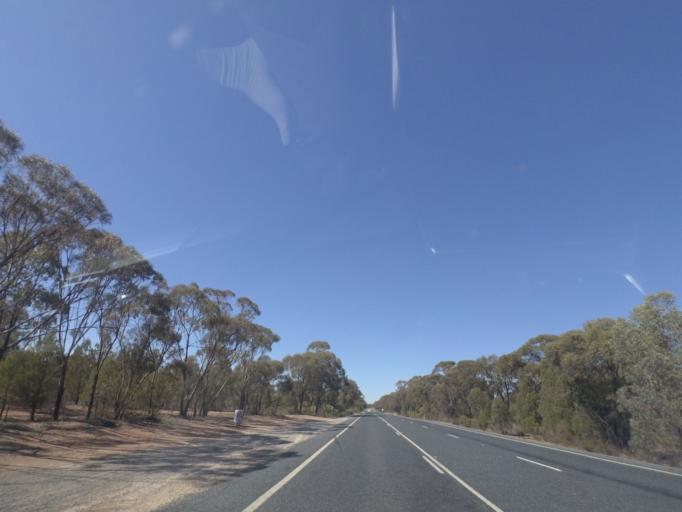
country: AU
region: New South Wales
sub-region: Bland
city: West Wyalong
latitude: -34.1308
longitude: 147.1236
